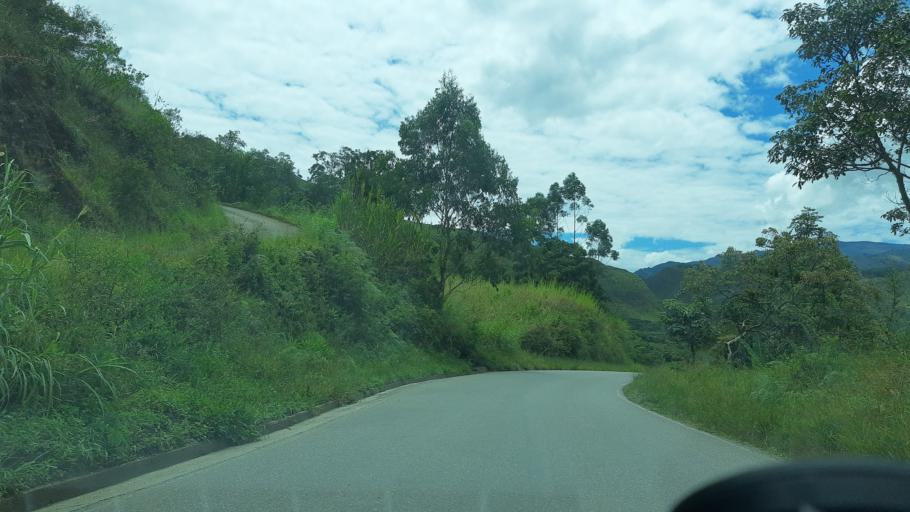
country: CO
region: Cundinamarca
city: Tenza
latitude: 5.0304
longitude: -73.3911
